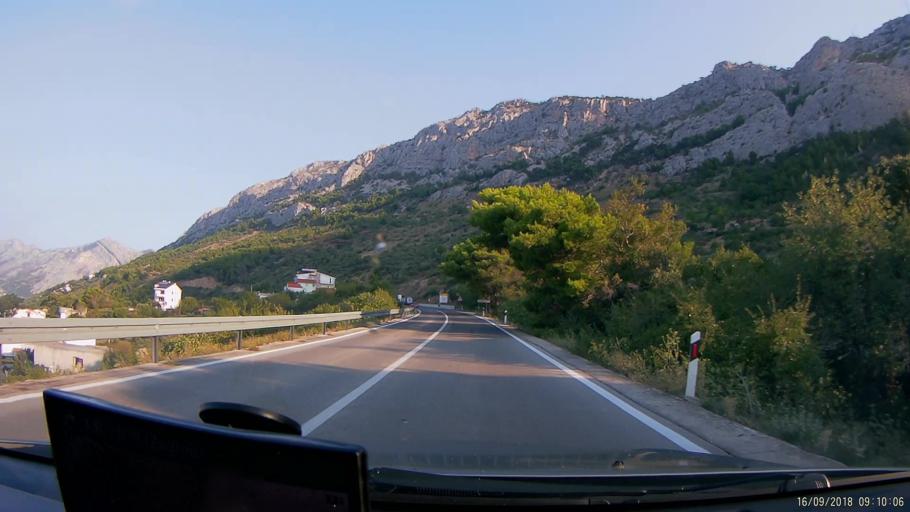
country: HR
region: Splitsko-Dalmatinska
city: Donja Brela
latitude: 43.3790
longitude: 16.9222
